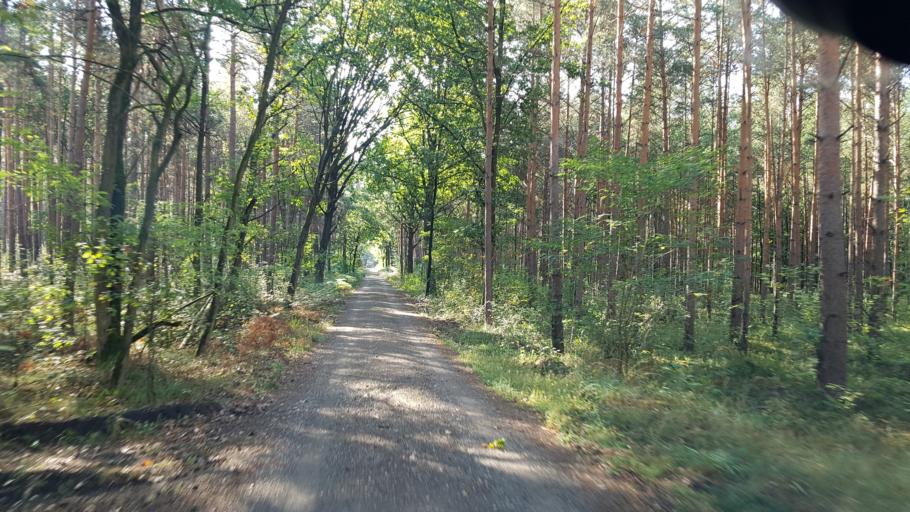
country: DE
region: Brandenburg
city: Plessa
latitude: 51.5265
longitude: 13.6379
